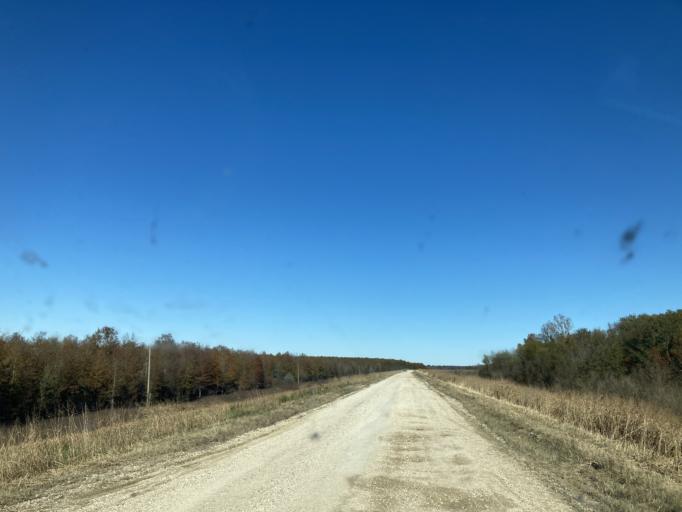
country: US
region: Mississippi
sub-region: Sharkey County
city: Rolling Fork
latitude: 32.7529
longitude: -90.6592
